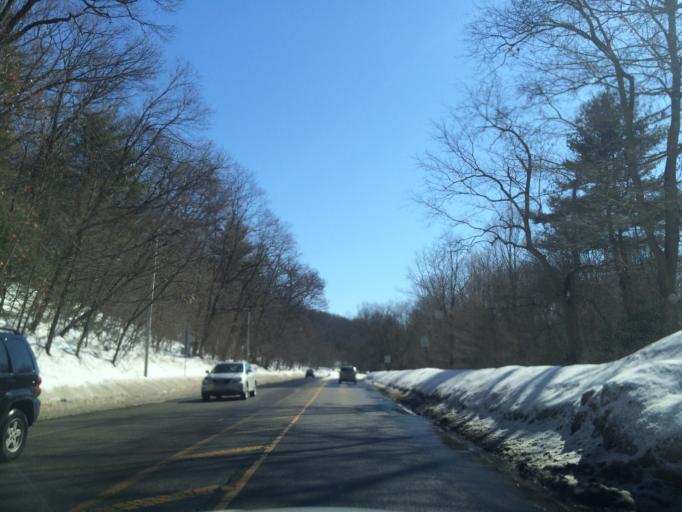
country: US
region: Massachusetts
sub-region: Norfolk County
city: Wellesley
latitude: 42.2978
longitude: -71.2775
